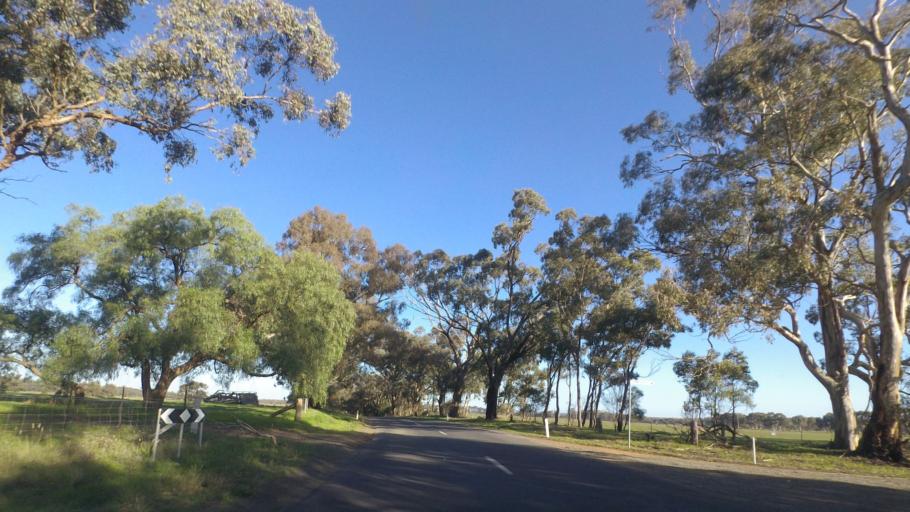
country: AU
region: Victoria
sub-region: Greater Bendigo
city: Epsom
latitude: -36.6684
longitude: 144.5208
